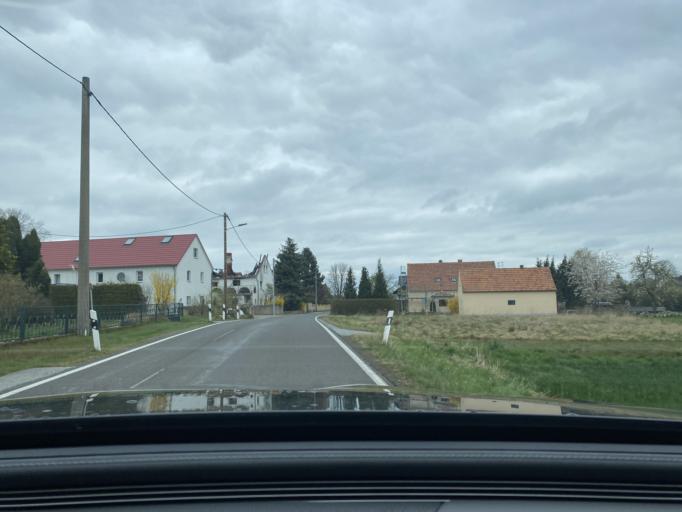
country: DE
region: Saxony
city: Neschwitz
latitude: 51.2519
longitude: 14.3339
